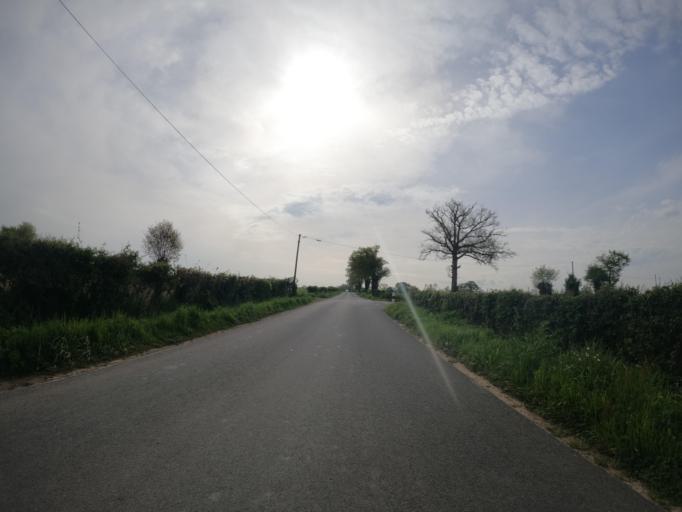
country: FR
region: Poitou-Charentes
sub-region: Departement des Deux-Sevres
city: Moncoutant
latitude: 46.6990
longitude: -0.5508
